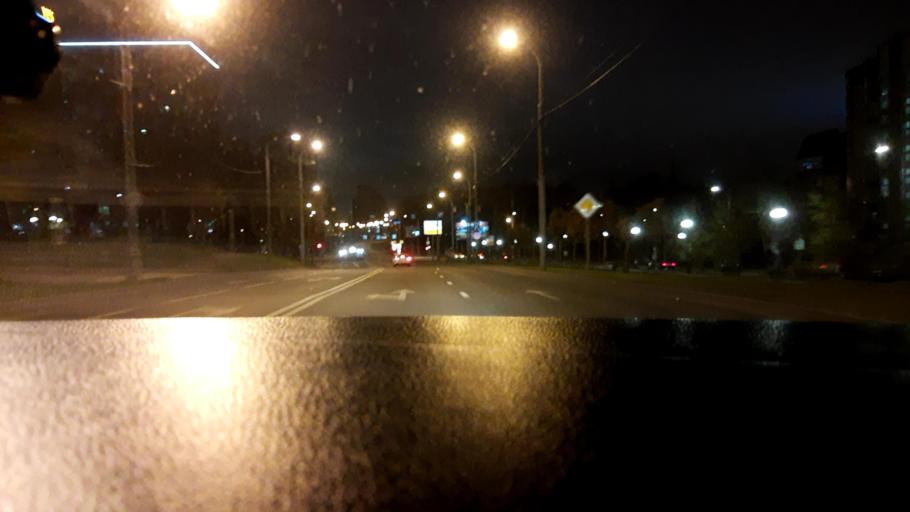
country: RU
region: Moskovskaya
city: Pavshino
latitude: 55.8428
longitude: 37.3693
